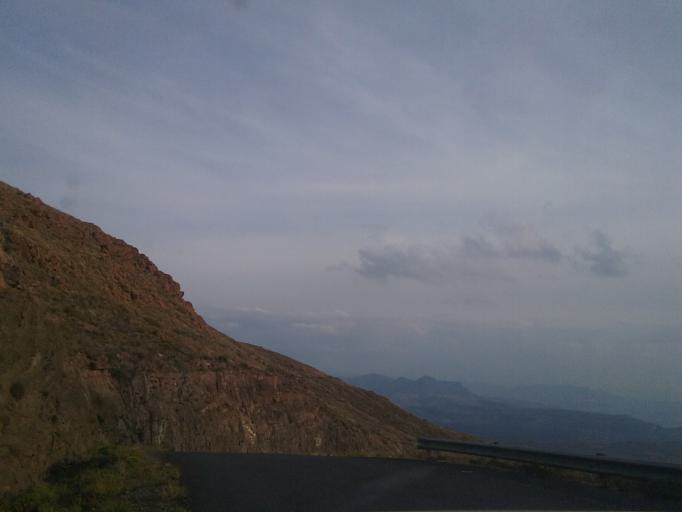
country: LS
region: Quthing
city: Quthing
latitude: -30.1878
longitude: 27.9695
